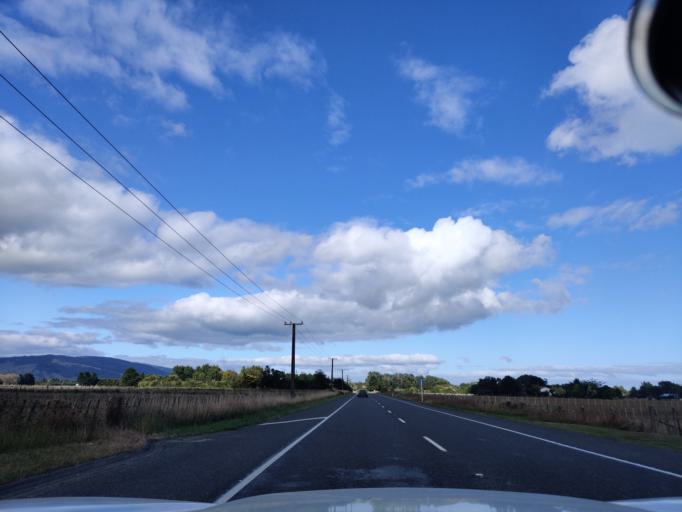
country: NZ
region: Manawatu-Wanganui
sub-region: Horowhenua District
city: Levin
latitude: -40.6458
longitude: 175.2906
